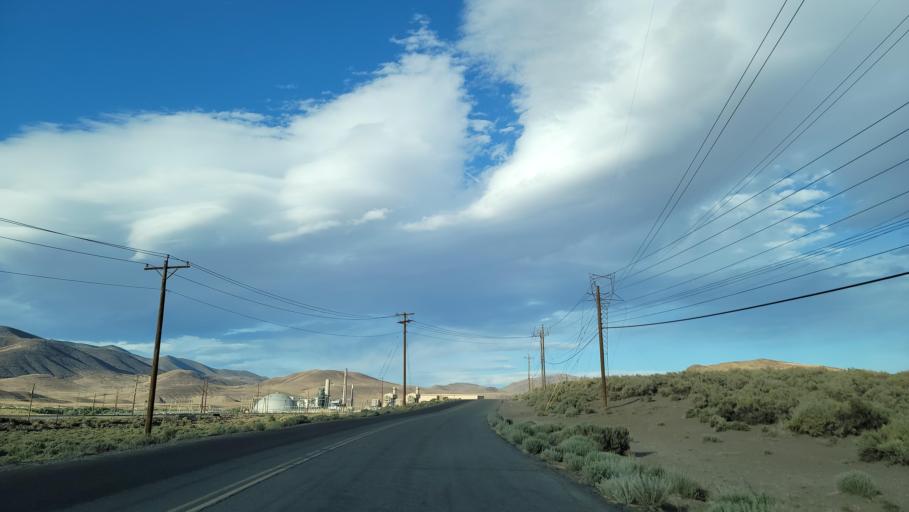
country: US
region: Nevada
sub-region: Washoe County
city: Spanish Springs
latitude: 39.5562
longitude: -119.5382
